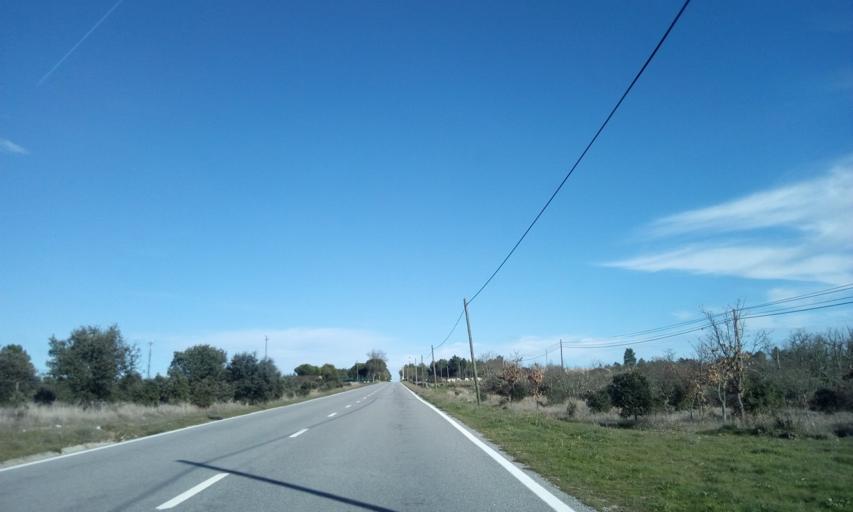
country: ES
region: Castille and Leon
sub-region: Provincia de Salamanca
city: Fuentes de Onoro
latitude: 40.6159
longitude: -6.8831
